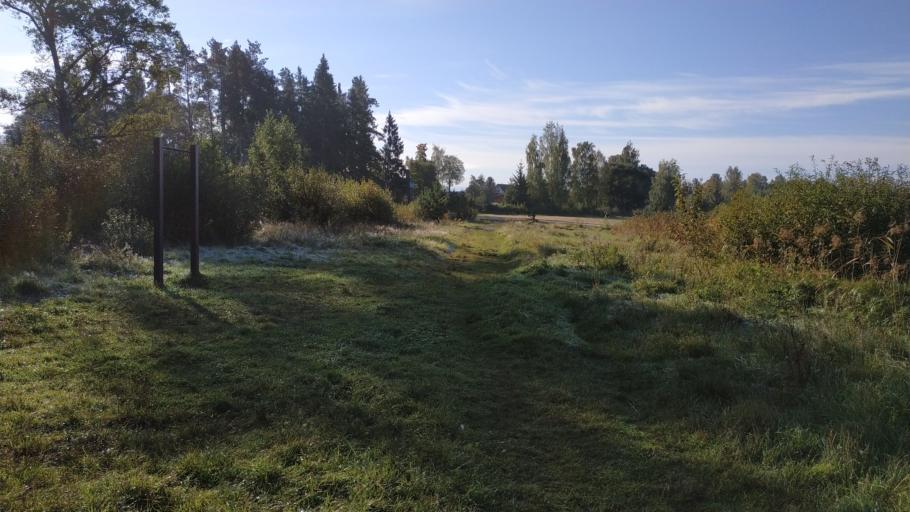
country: BY
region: Vitebsk
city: Vitebsk
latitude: 55.0906
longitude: 30.1650
